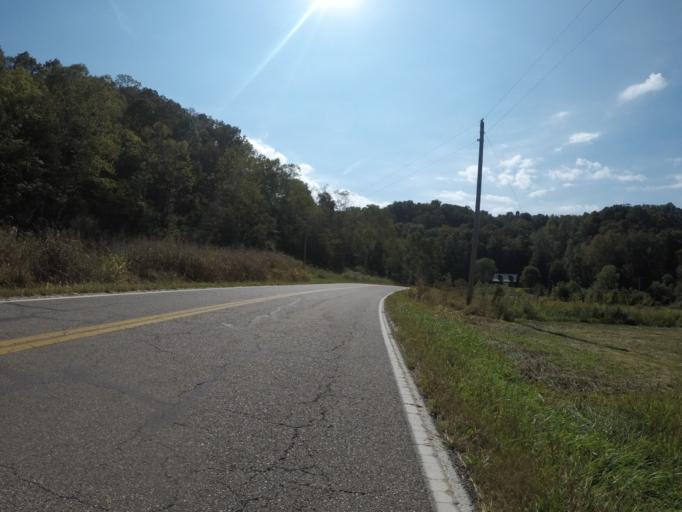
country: US
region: West Virginia
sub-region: Cabell County
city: Lesage
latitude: 38.6363
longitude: -82.4310
